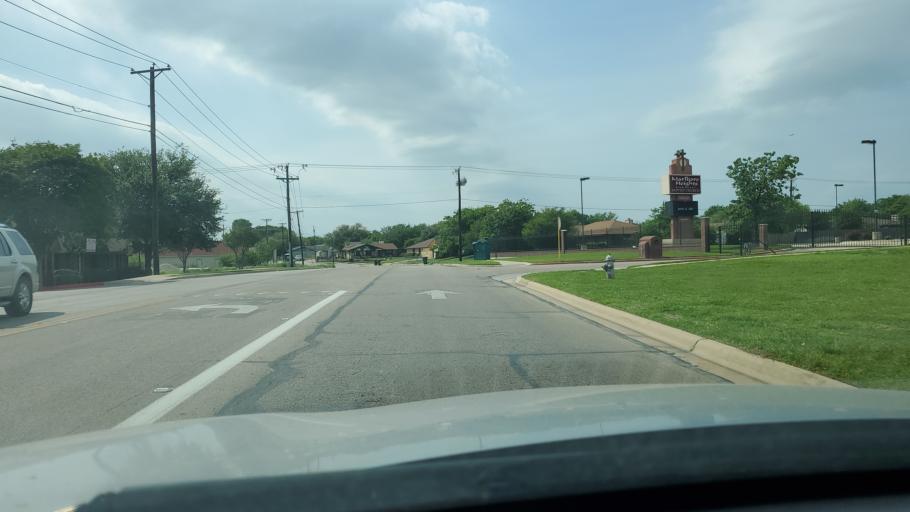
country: US
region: Texas
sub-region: Bell County
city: Killeen
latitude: 31.0927
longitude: -97.7106
